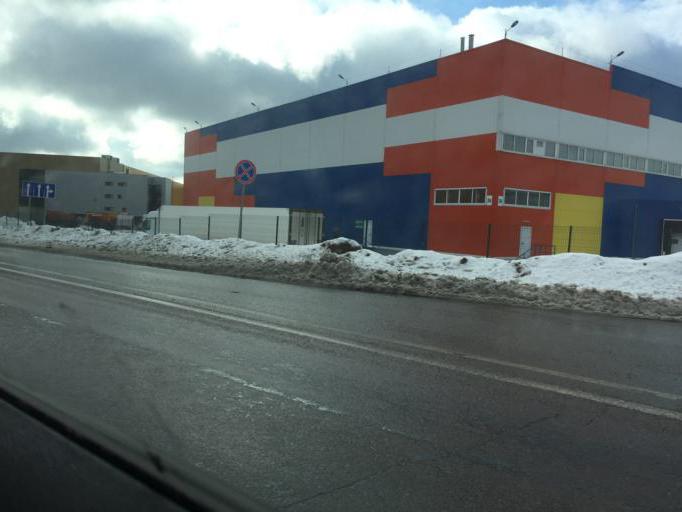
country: RU
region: Moskovskaya
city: Pavlovskaya Sloboda
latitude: 55.8182
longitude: 37.1142
